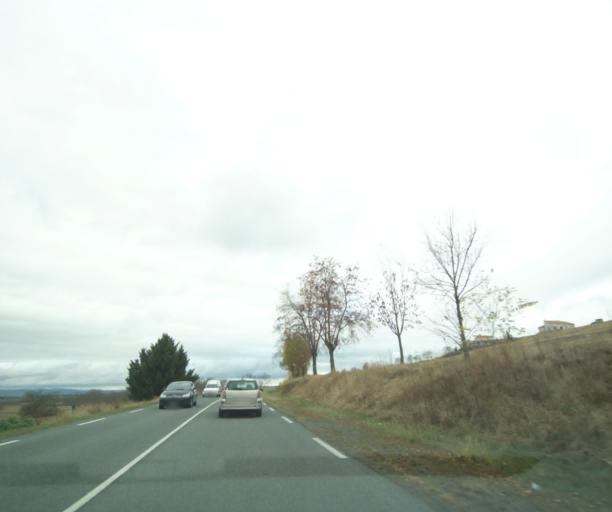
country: FR
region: Auvergne
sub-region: Departement du Puy-de-Dome
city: Pont-du-Chateau
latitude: 45.7994
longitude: 3.2265
